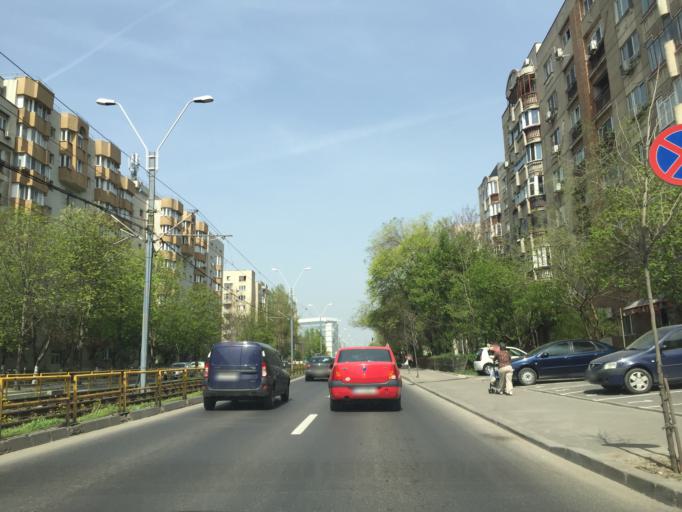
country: RO
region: Ilfov
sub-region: Comuna Chiajna
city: Rosu
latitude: 44.4389
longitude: 26.0354
